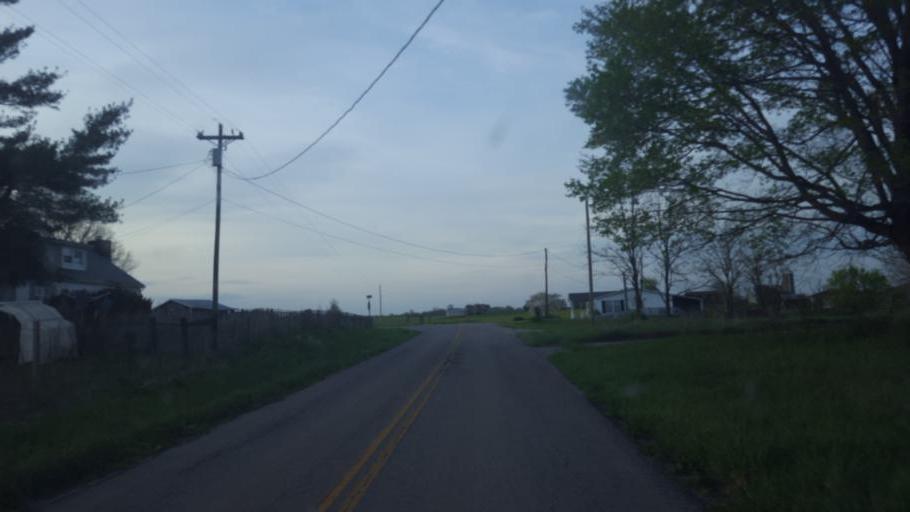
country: US
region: Kentucky
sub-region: Metcalfe County
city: Edmonton
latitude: 37.1164
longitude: -85.6976
